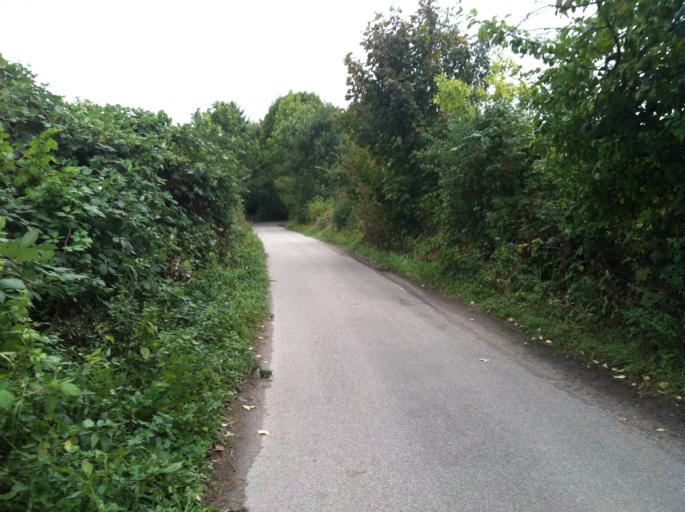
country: DE
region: Rheinland-Pfalz
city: Budenheim
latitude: 50.0303
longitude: 8.1998
